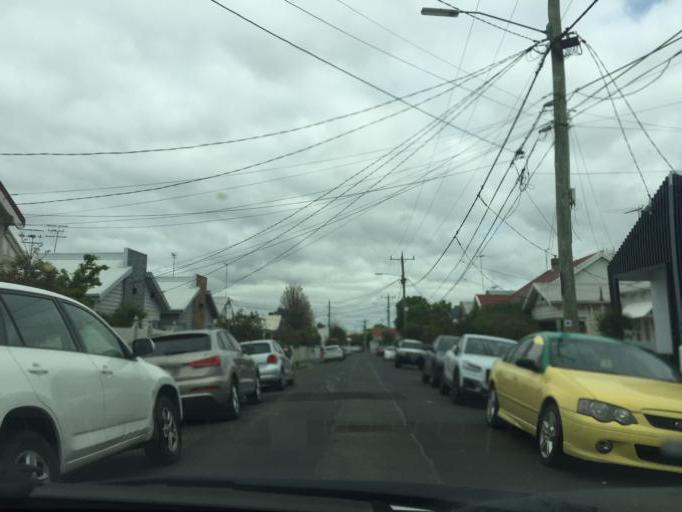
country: AU
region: Victoria
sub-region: Maribyrnong
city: Seddon
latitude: -37.8150
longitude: 144.8891
